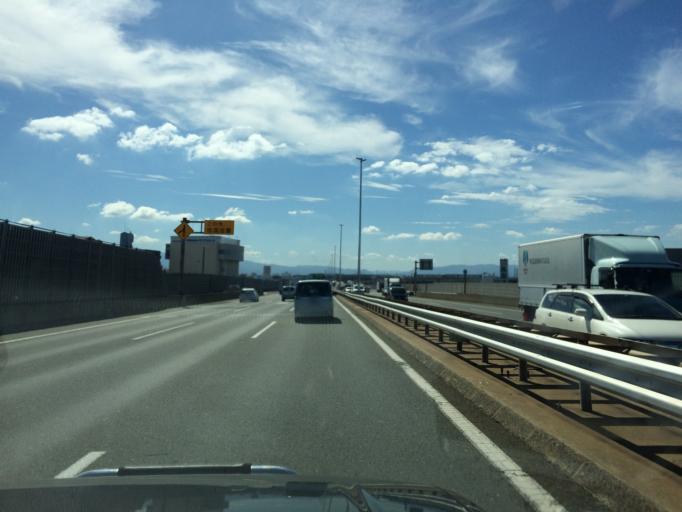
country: JP
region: Osaka
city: Yao
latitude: 34.5994
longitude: 135.5742
